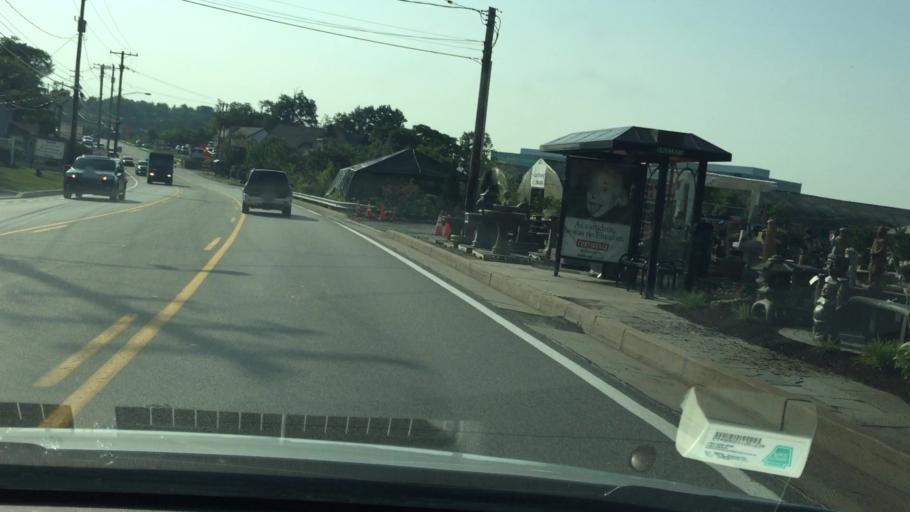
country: US
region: Pennsylvania
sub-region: Allegheny County
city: Rennerdale
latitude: 40.4496
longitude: -80.1259
